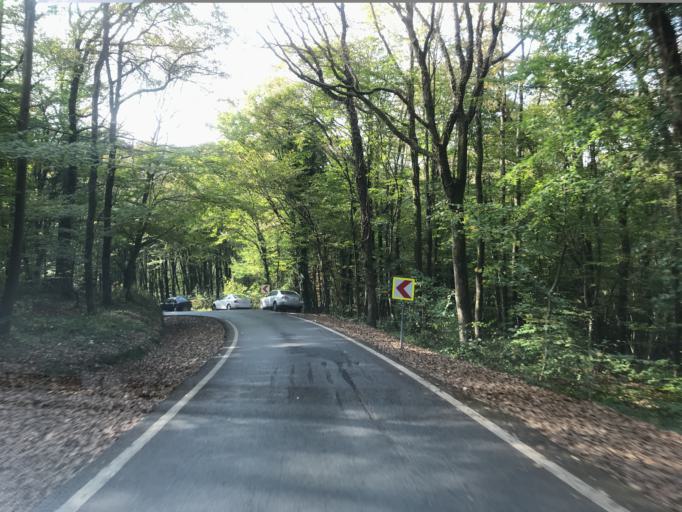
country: TR
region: Istanbul
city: Arikoey
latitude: 41.1896
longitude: 28.9708
